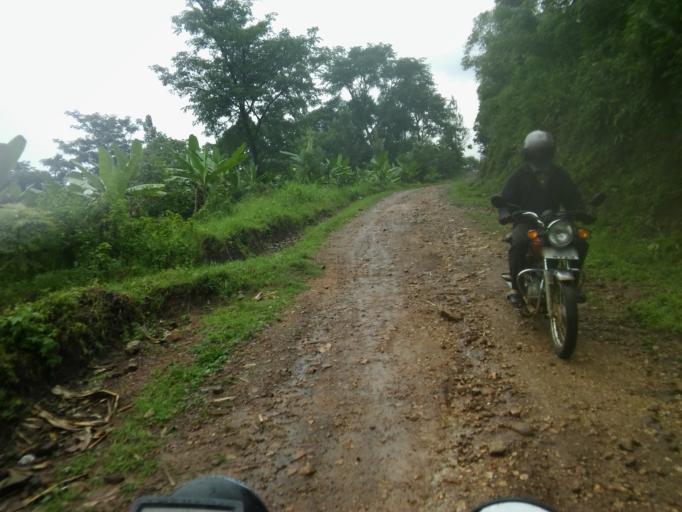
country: UG
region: Eastern Region
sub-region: Bududa District
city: Bududa
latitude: 0.9982
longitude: 34.2371
